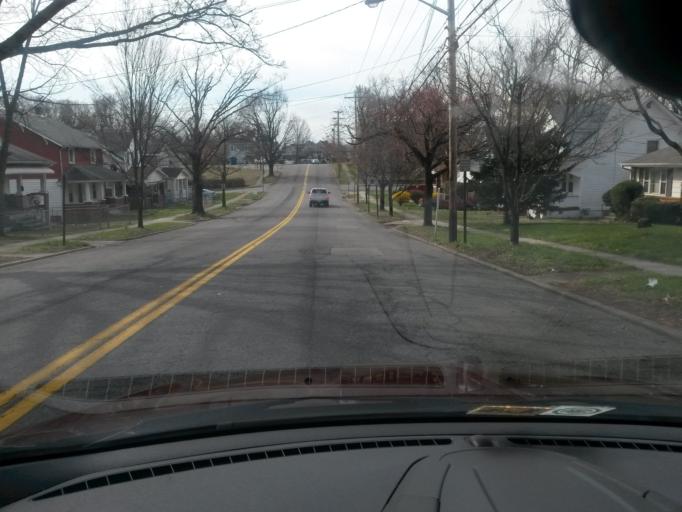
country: US
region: Virginia
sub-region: City of Roanoke
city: Roanoke
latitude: 37.2919
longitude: -79.9757
